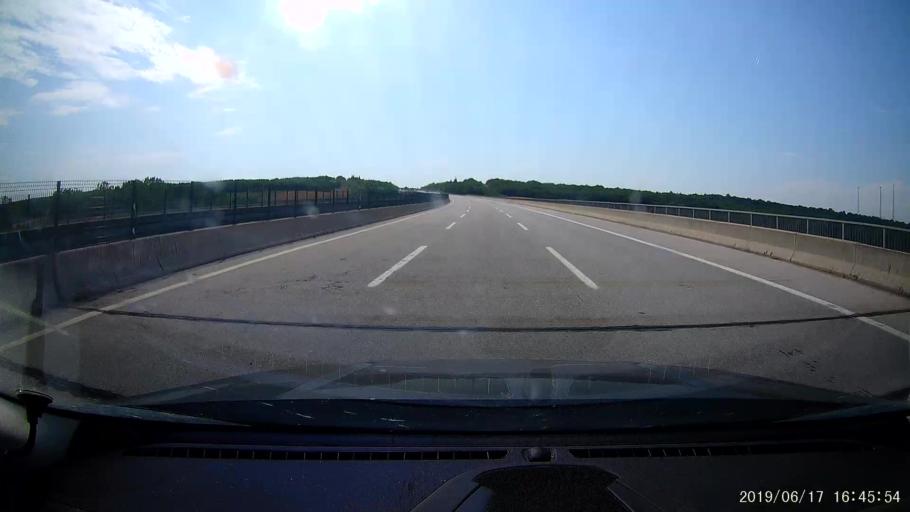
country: TR
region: Kirklareli
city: Babaeski
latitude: 41.4943
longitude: 27.2198
